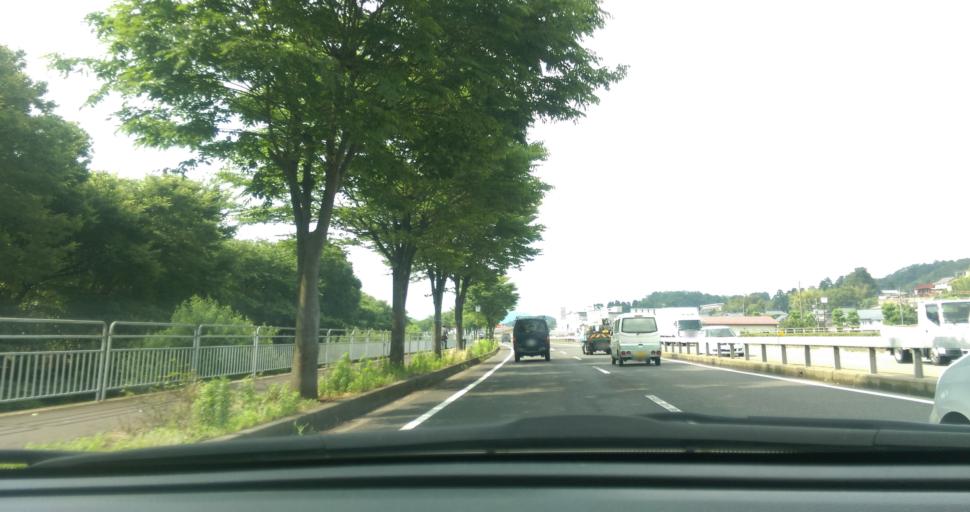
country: JP
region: Fukui
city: Sabae
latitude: 35.9607
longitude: 136.1883
